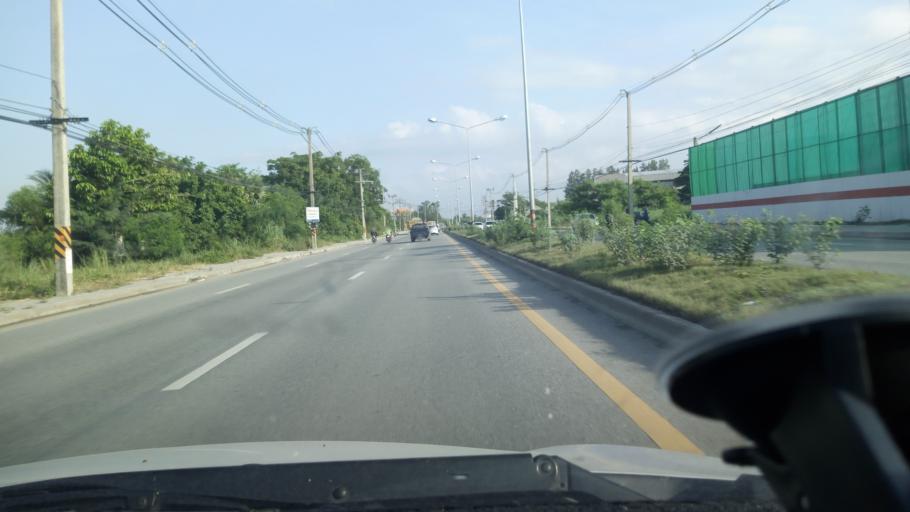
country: TH
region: Chon Buri
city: Phan Thong
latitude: 13.4473
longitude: 101.1014
